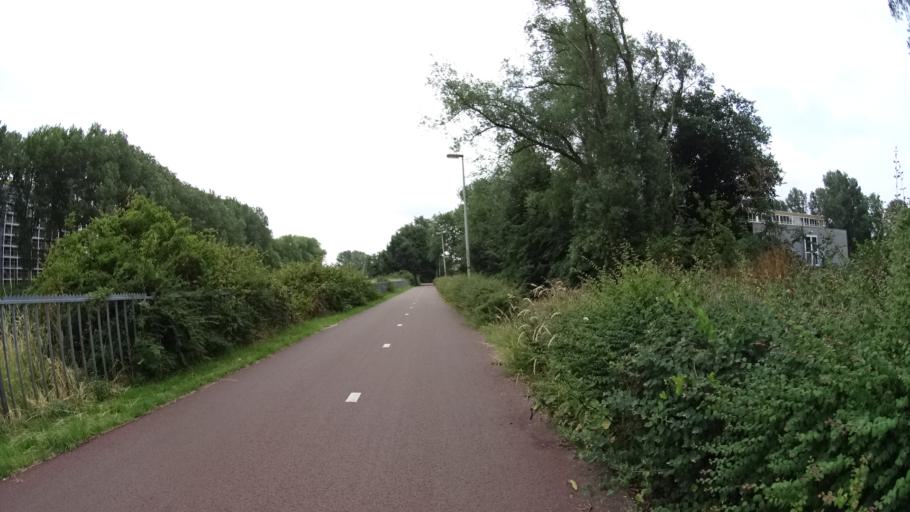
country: NL
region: South Holland
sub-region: Gemeente Den Haag
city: Scheveningen
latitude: 52.0845
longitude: 4.2734
